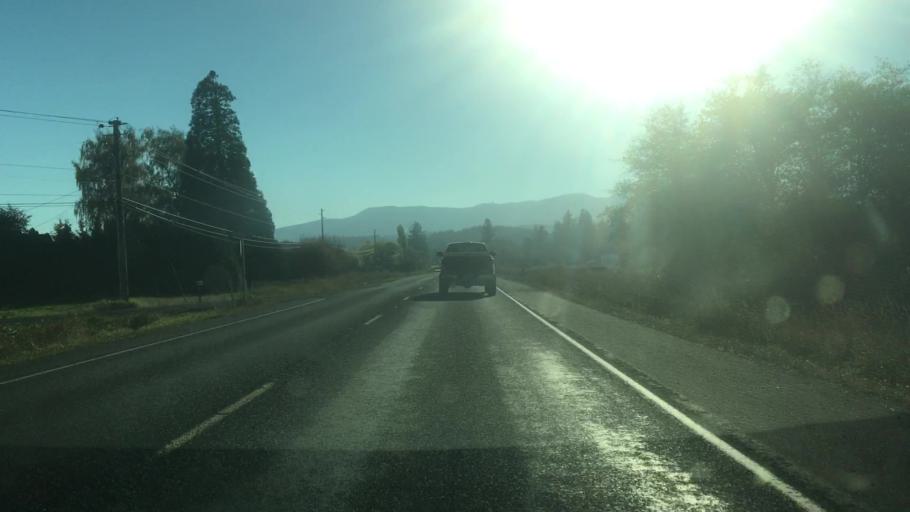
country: US
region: Oregon
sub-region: Clatsop County
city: Astoria
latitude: 46.3720
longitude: -123.8053
